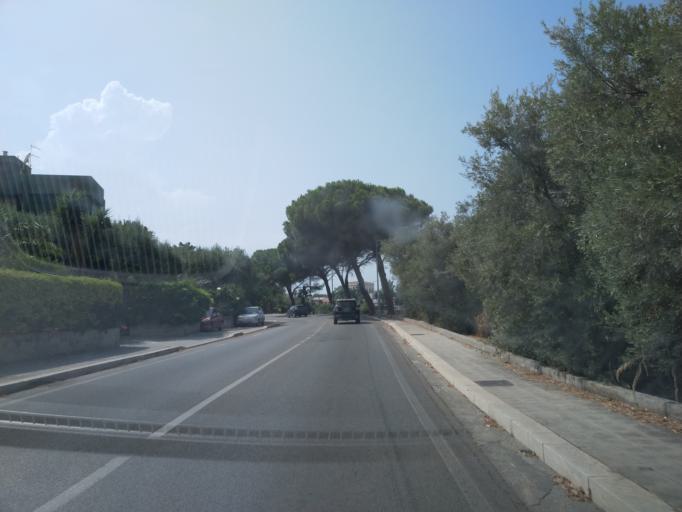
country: IT
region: Sicily
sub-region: Palermo
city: Cefalu
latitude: 38.0313
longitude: 14.0039
